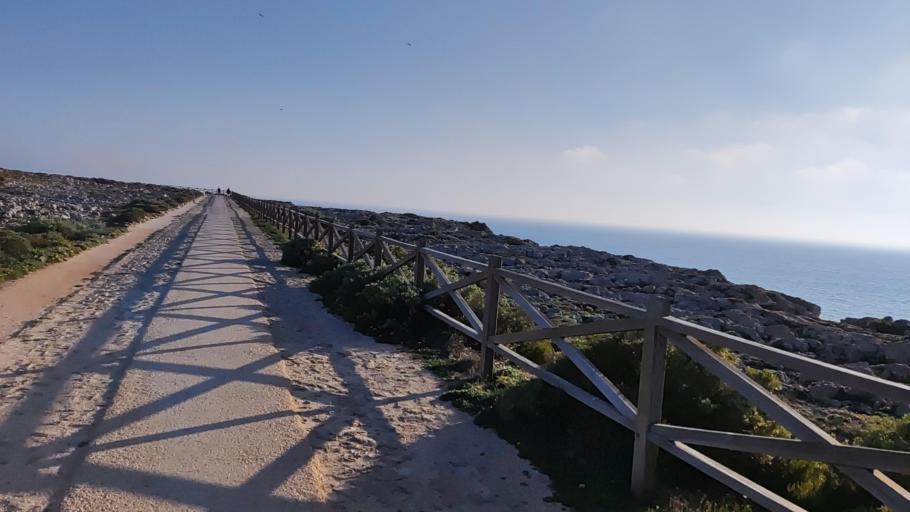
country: PT
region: Faro
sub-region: Vila do Bispo
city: Sagres
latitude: 36.9995
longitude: -8.9506
